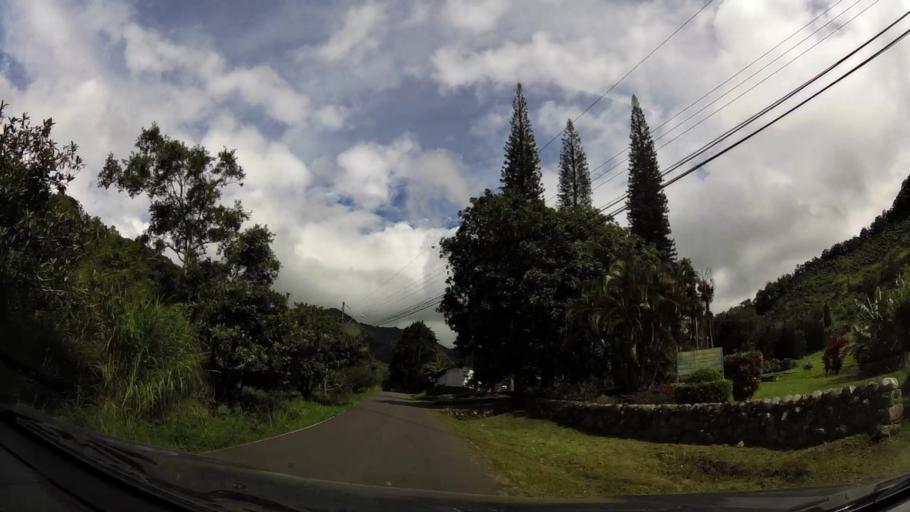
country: PA
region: Chiriqui
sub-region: Distrito Boquete
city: Boquete
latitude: 8.7939
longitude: -82.4284
